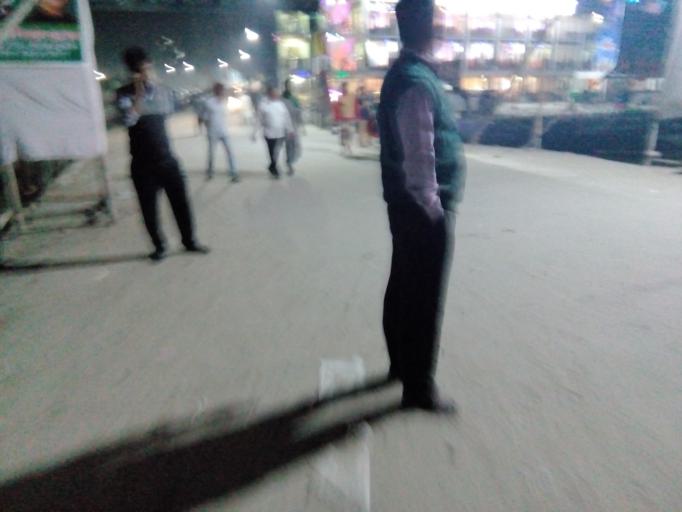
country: BD
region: Dhaka
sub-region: Dhaka
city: Dhaka
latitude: 23.6933
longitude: 90.4755
